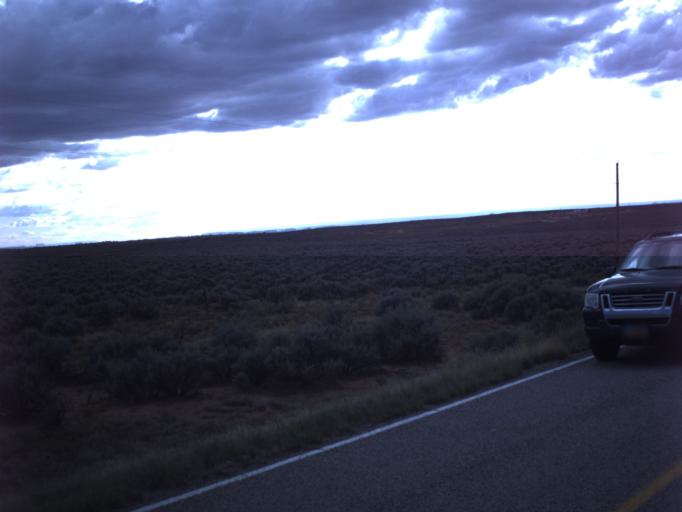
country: US
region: Utah
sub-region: San Juan County
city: Blanding
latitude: 37.4230
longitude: -109.3408
